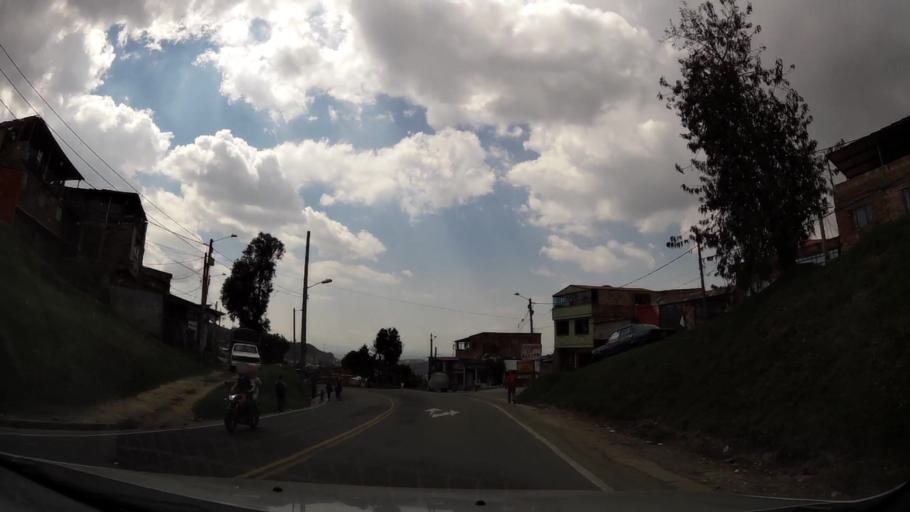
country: CO
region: Bogota D.C.
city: Bogota
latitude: 4.5553
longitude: -74.0930
